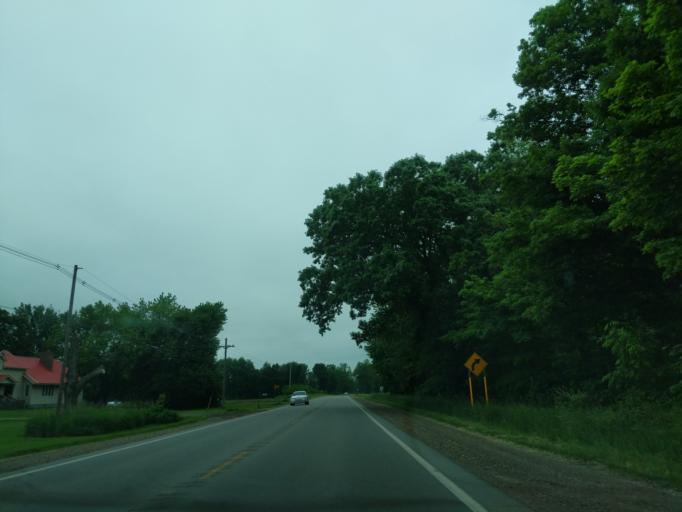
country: US
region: Michigan
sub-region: Branch County
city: Quincy
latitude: 41.9493
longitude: -84.8083
